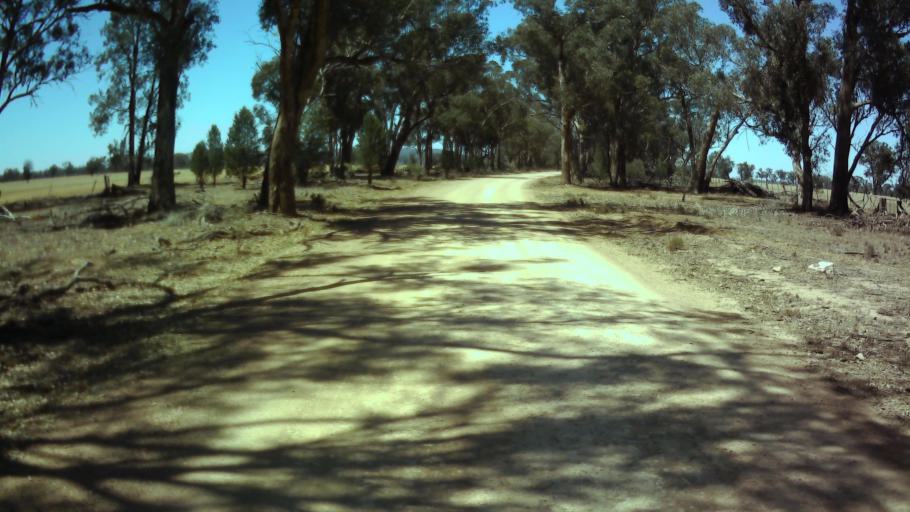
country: AU
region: New South Wales
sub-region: Weddin
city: Grenfell
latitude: -34.0340
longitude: 148.0139
